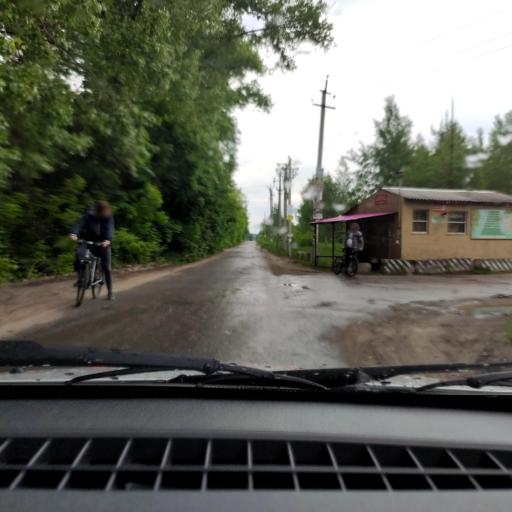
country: RU
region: Voronezj
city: Ramon'
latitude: 51.8501
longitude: 39.2377
